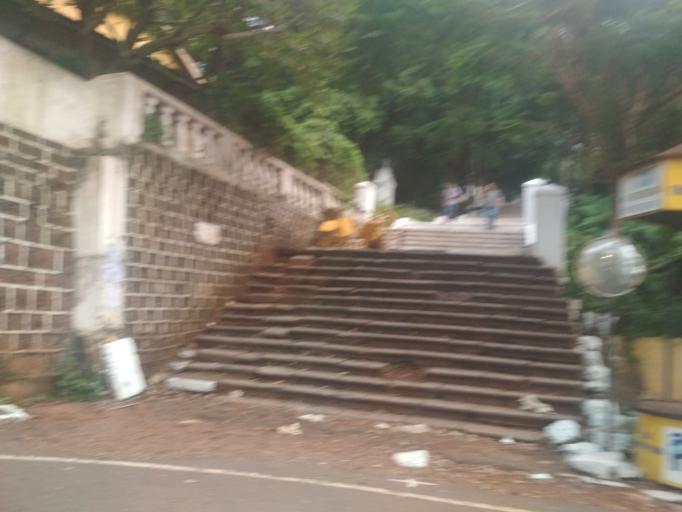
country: IN
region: Goa
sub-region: North Goa
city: Panaji
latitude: 15.4946
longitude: 73.8271
